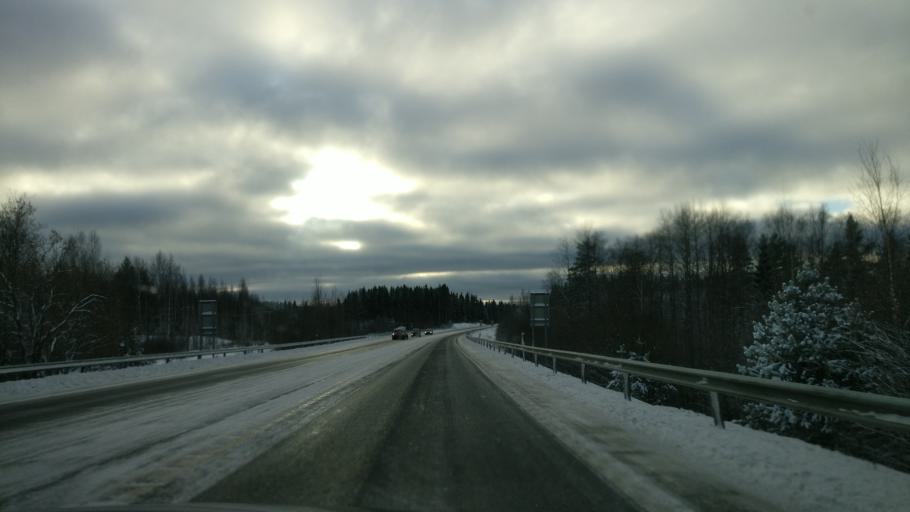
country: FI
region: Southern Savonia
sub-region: Mikkeli
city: Pertunmaa
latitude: 61.3773
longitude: 26.3007
